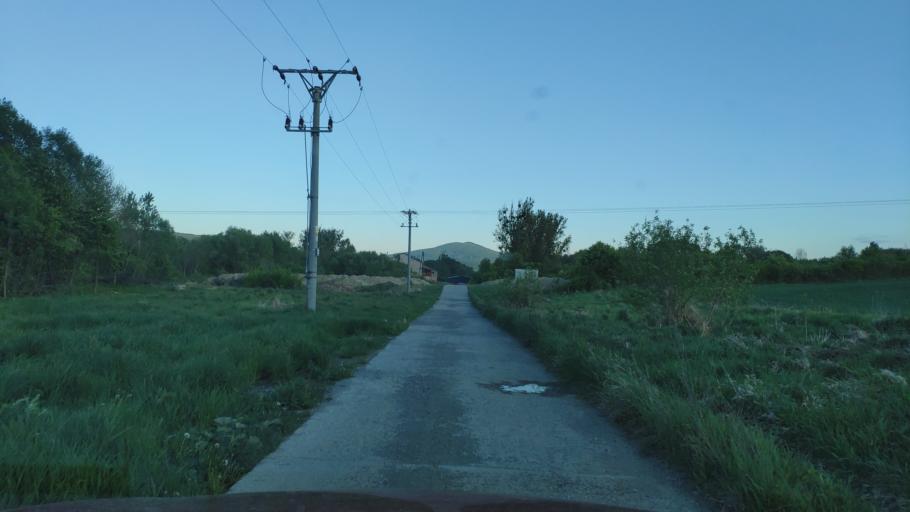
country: SK
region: Kosicky
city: Kosice
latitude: 48.7342
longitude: 21.4206
